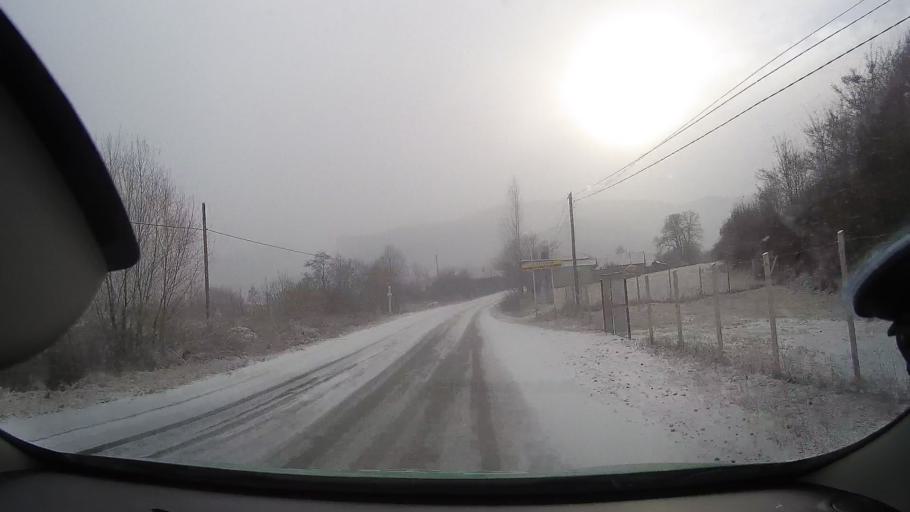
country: RO
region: Alba
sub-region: Comuna Rimetea
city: Rimetea
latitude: 46.3928
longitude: 23.5610
